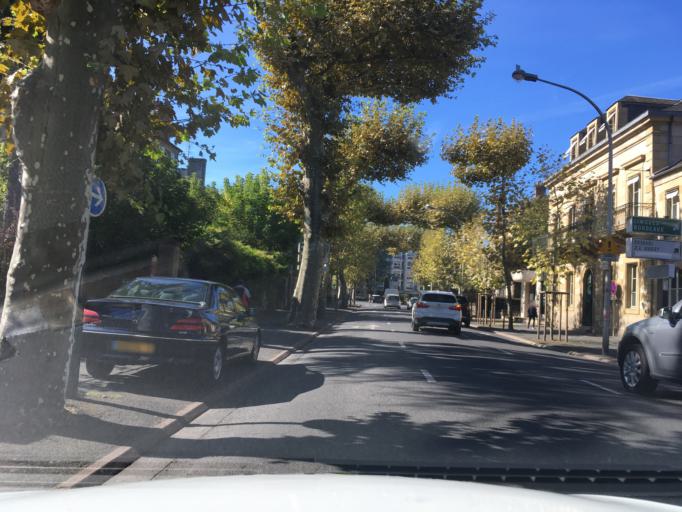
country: FR
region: Limousin
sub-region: Departement de la Correze
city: Brive-la-Gaillarde
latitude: 45.1600
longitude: 1.5314
